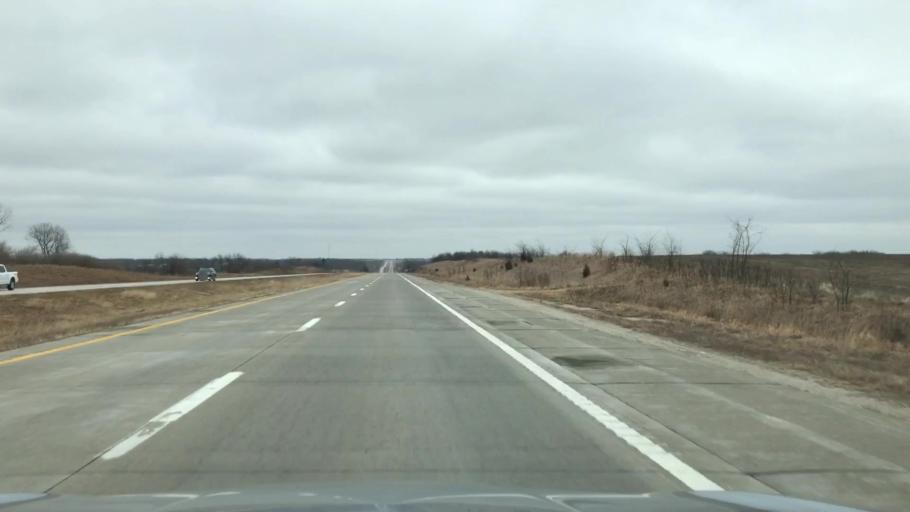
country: US
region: Missouri
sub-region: Caldwell County
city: Hamilton
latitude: 39.7347
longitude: -93.8479
